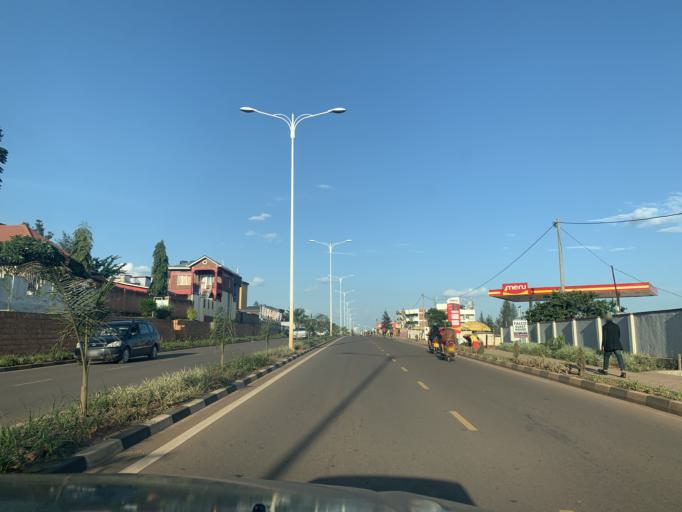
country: RW
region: Kigali
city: Kigali
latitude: -1.9618
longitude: 30.1112
